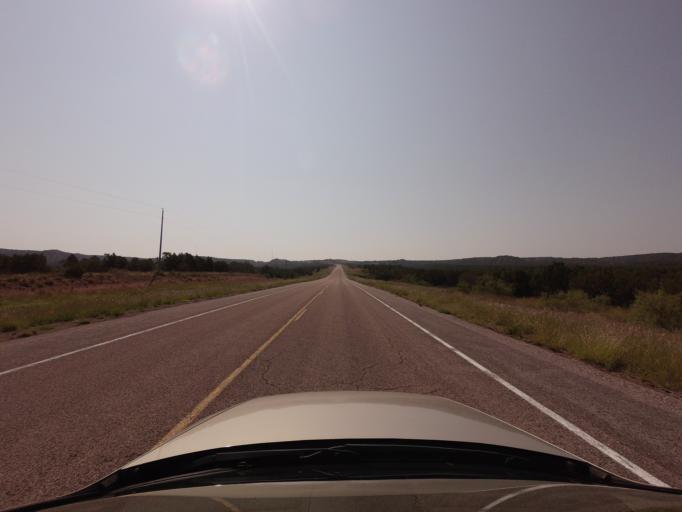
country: US
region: New Mexico
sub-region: Quay County
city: Tucumcari
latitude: 34.8324
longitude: -103.7554
